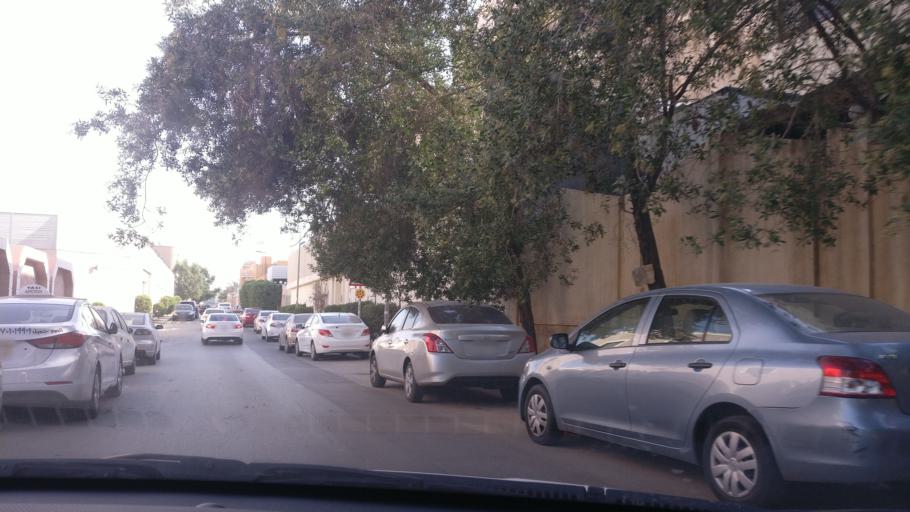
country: SA
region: Ar Riyad
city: Riyadh
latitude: 24.7028
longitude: 46.6837
